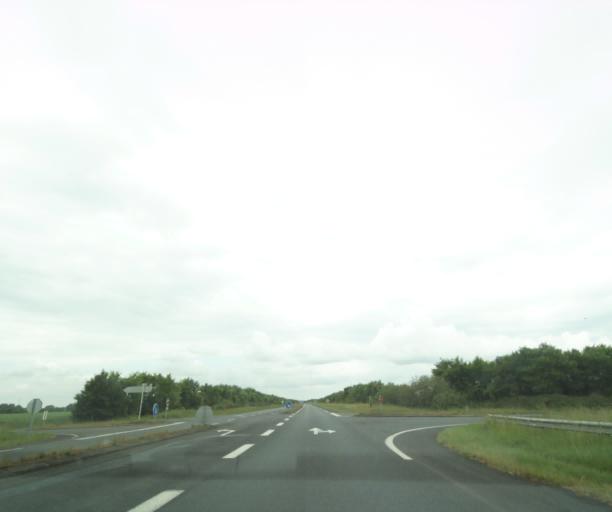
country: FR
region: Poitou-Charentes
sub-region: Departement des Deux-Sevres
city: Saint-Varent
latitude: 46.8756
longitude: -0.1966
